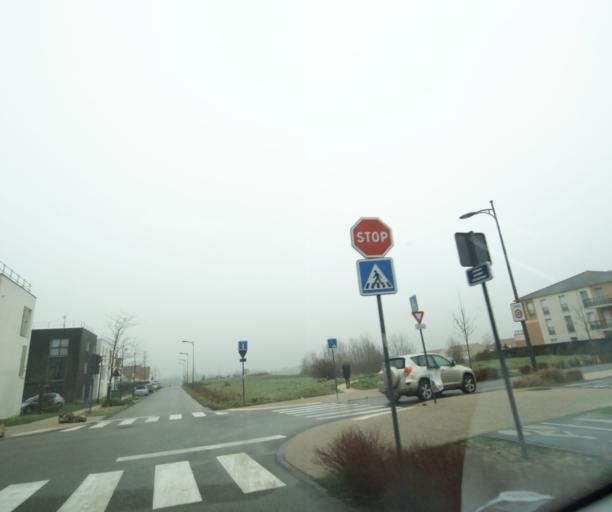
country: FR
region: Ile-de-France
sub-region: Departement de Seine-et-Marne
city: Dammartin-en-Goele
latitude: 49.0638
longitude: 2.6767
